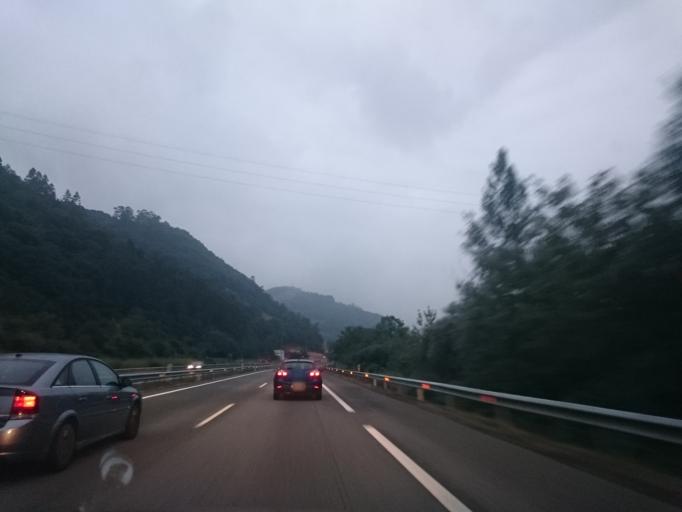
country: ES
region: Asturias
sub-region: Province of Asturias
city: Mieres
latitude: 43.2201
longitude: -5.7839
